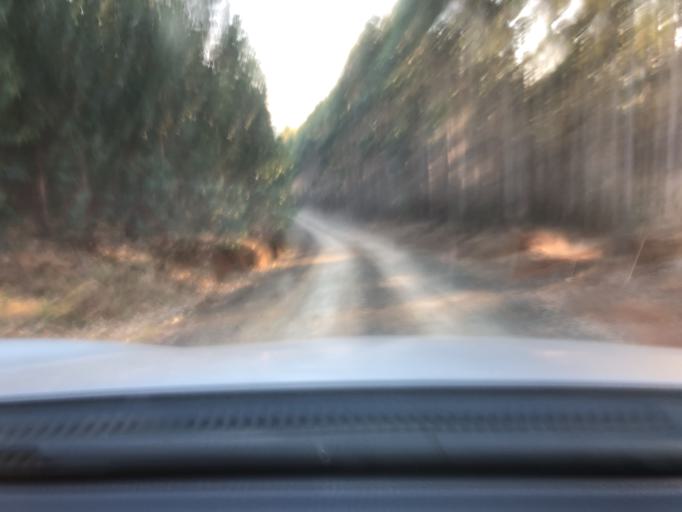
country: ZA
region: KwaZulu-Natal
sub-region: Sisonke District Municipality
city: Ixopo
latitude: -30.1823
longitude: 30.0558
